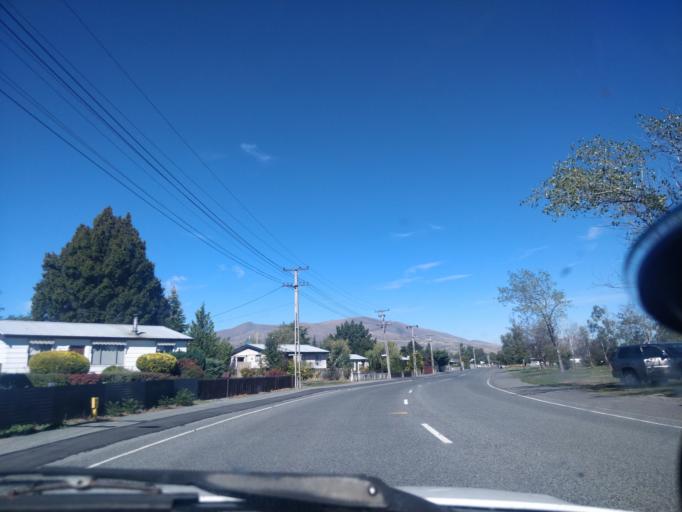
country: NZ
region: Canterbury
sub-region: Timaru District
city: Pleasant Point
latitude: -44.2541
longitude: 170.1015
